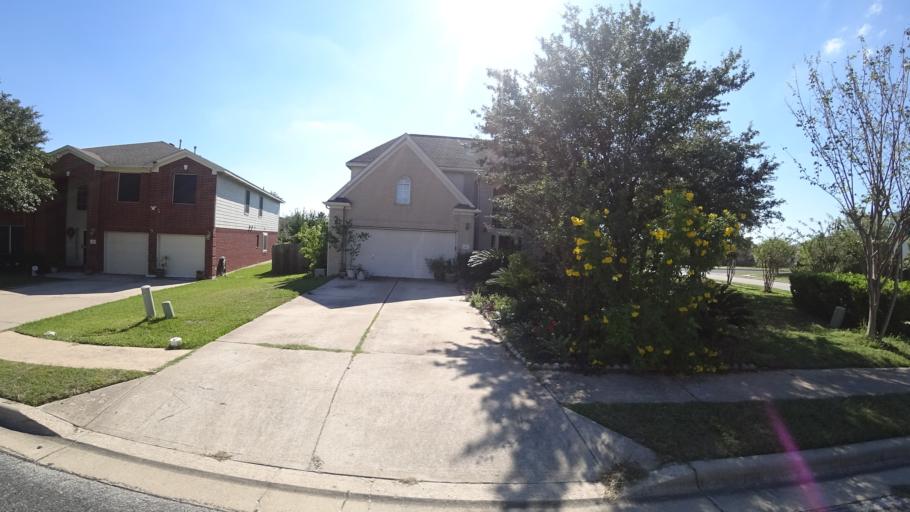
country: US
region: Texas
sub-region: Travis County
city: Manor
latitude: 30.3511
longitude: -97.6096
